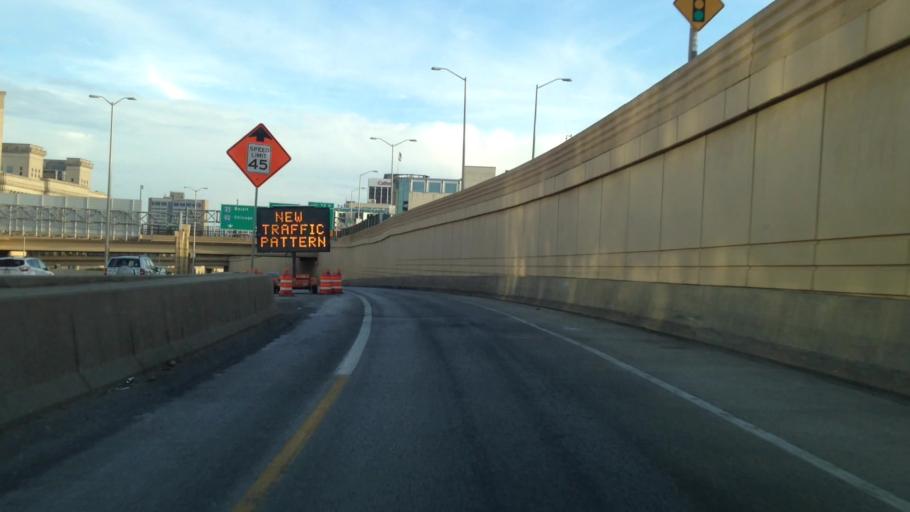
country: US
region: Wisconsin
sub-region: Milwaukee County
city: Milwaukee
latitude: 43.0461
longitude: -87.9268
